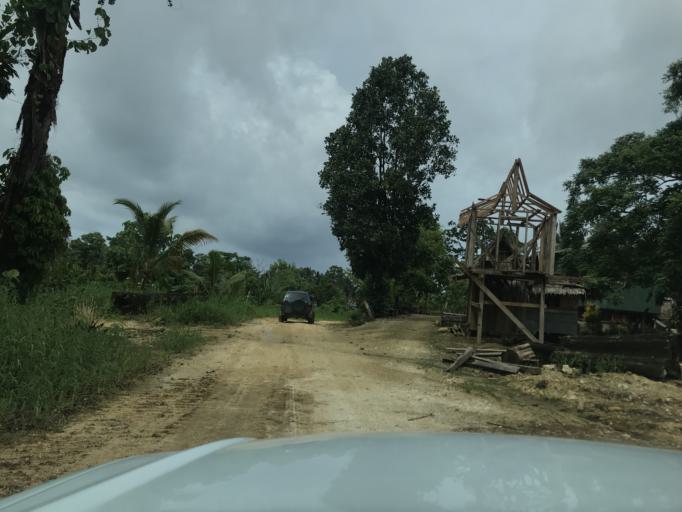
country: SB
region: Malaita
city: Auki
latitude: -8.6312
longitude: 160.6624
